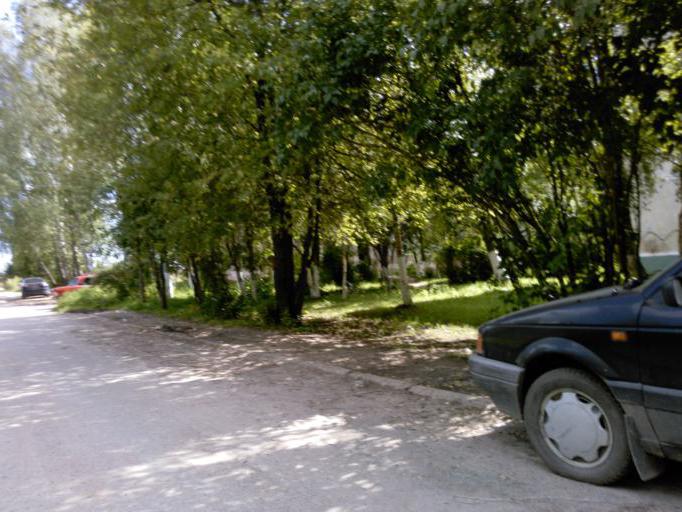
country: RU
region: Moskovskaya
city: Solnechnogorsk
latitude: 56.1403
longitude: 36.8984
